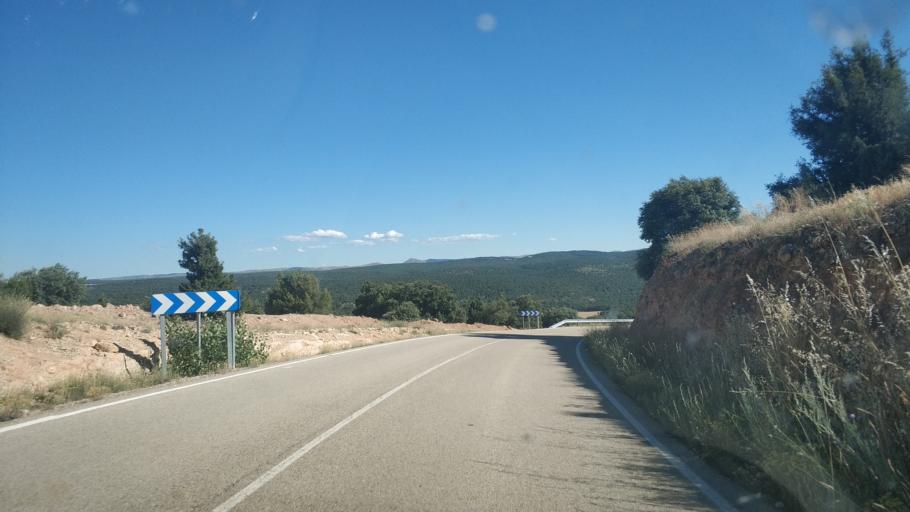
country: ES
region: Castille and Leon
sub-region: Provincia de Soria
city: Liceras
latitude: 41.4487
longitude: -3.2145
